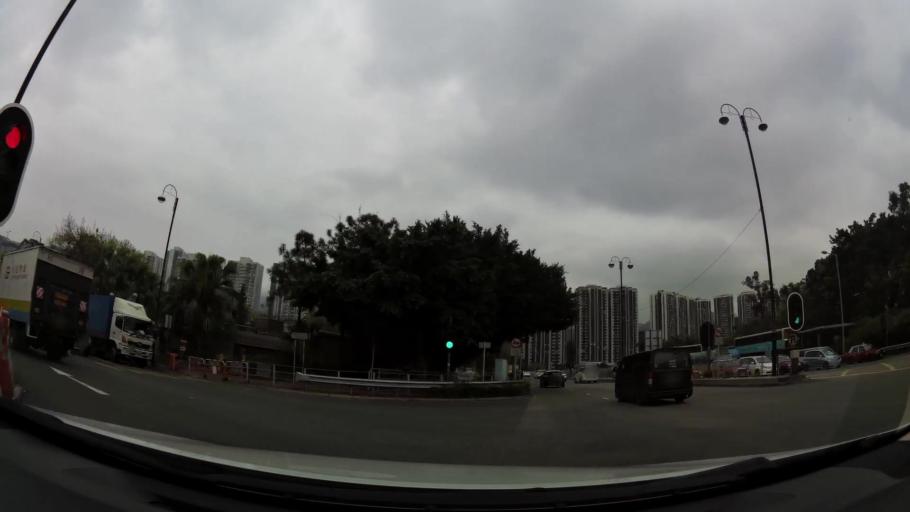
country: HK
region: Sha Tin
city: Sha Tin
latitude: 22.3891
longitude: 114.1983
